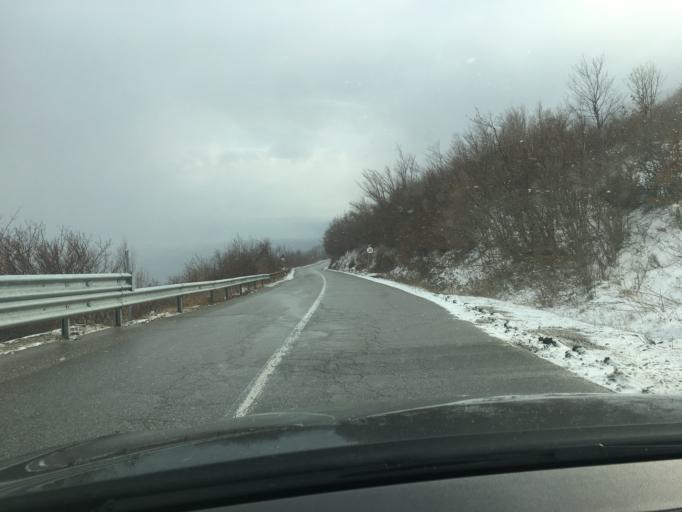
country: XK
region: Pec
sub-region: Komuna e Pejes
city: Dubova (Driloni)
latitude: 42.7584
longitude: 20.3006
